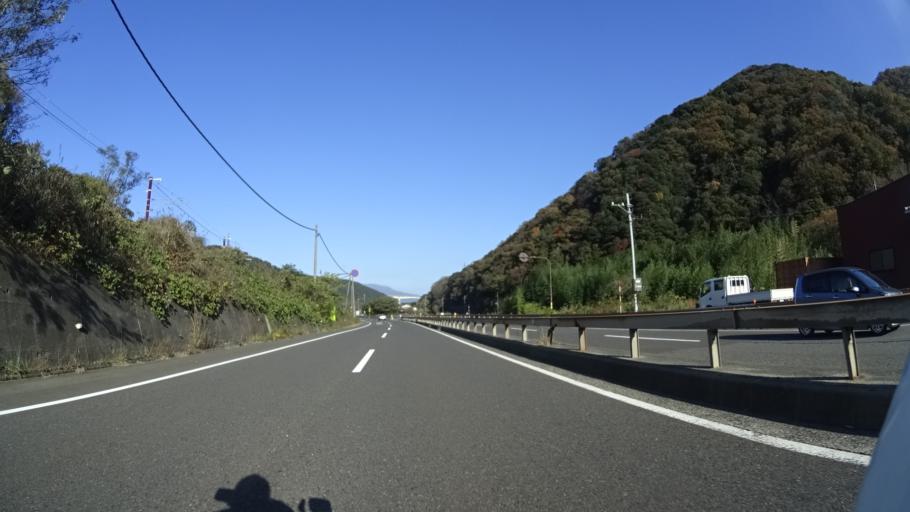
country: JP
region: Fukui
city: Tsuruga
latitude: 35.6076
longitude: 136.0879
